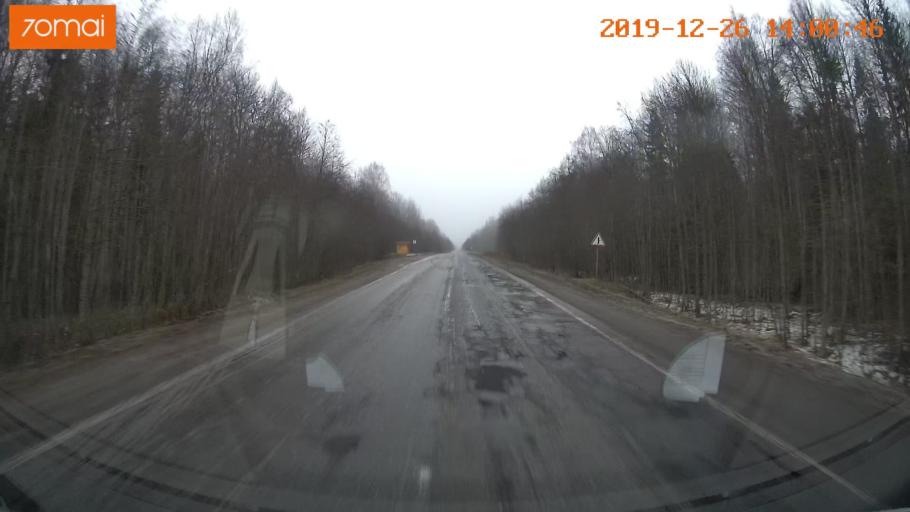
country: RU
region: Jaroslavl
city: Poshekhon'ye
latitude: 58.5556
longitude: 38.7501
